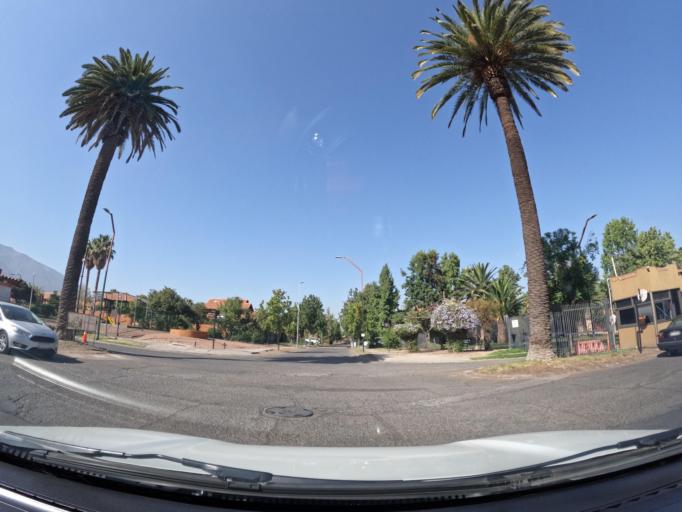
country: CL
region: Santiago Metropolitan
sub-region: Provincia de Santiago
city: Villa Presidente Frei, Nunoa, Santiago, Chile
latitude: -33.4826
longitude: -70.5511
